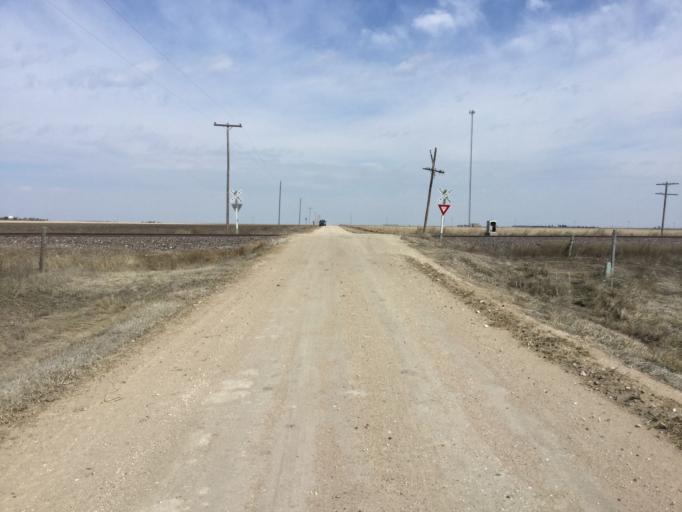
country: US
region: Kansas
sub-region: Lane County
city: Dighton
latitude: 38.5949
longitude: -100.6323
